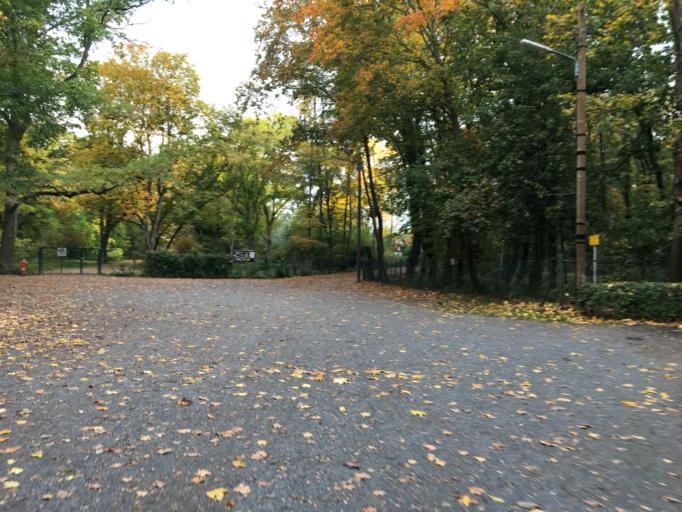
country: DE
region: Lower Saxony
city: Braunschweig
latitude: 52.2909
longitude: 10.5336
